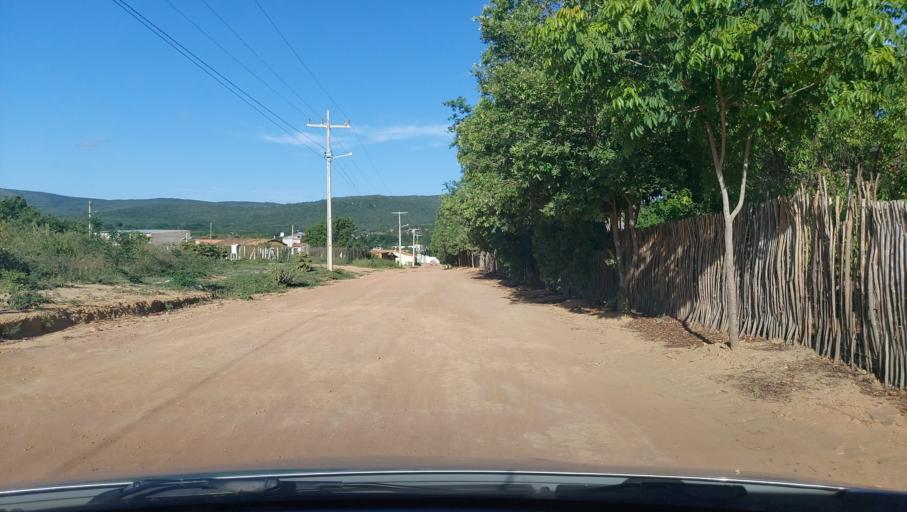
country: BR
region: Bahia
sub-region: Oliveira Dos Brejinhos
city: Beira Rio
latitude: -12.0031
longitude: -42.6308
